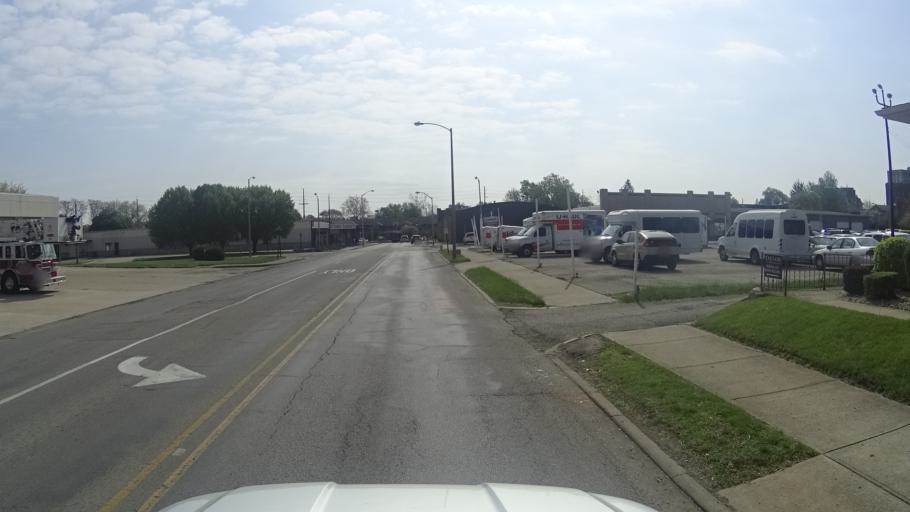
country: US
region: Indiana
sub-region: Madison County
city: Anderson
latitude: 40.1108
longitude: -85.6801
